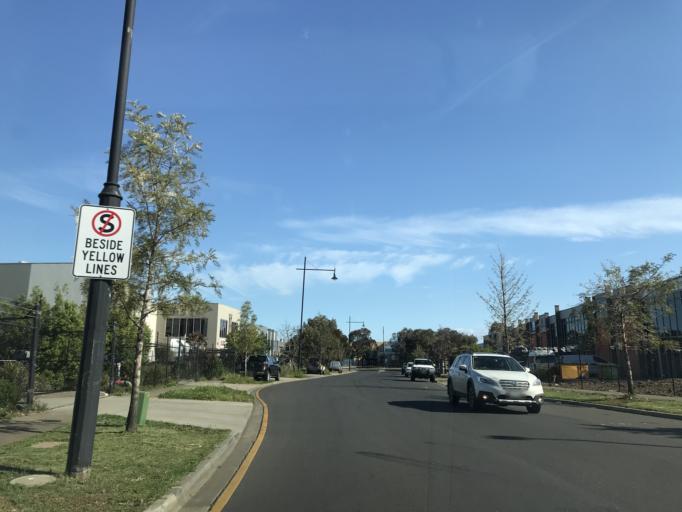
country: AU
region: Victoria
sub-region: Wyndham
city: Truganina
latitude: -37.8056
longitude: 144.7562
